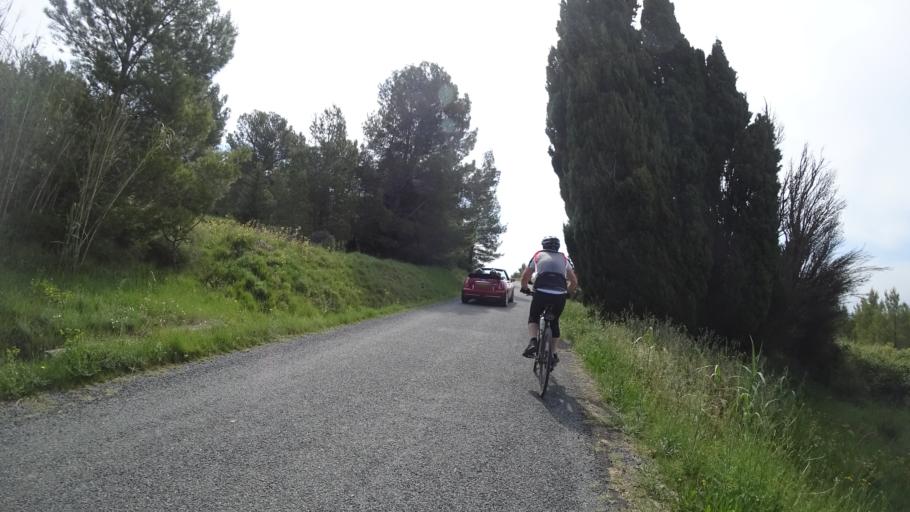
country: FR
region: Languedoc-Roussillon
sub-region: Departement de l'Aude
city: Canet
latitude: 43.2558
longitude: 2.8020
